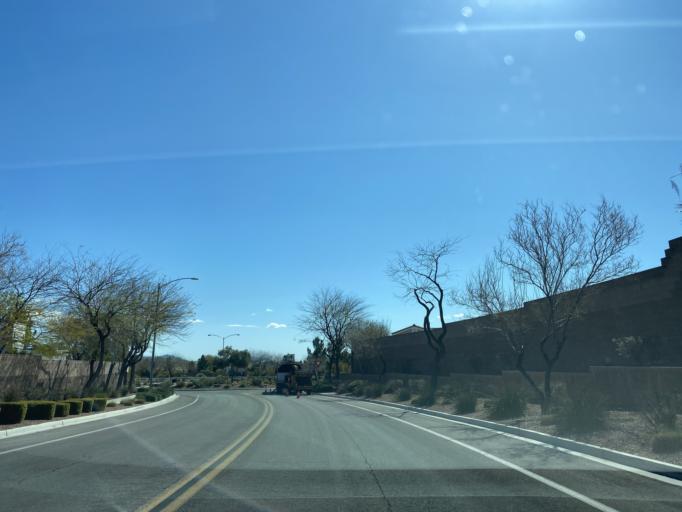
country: US
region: Nevada
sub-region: Clark County
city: North Las Vegas
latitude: 36.3305
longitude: -115.2705
